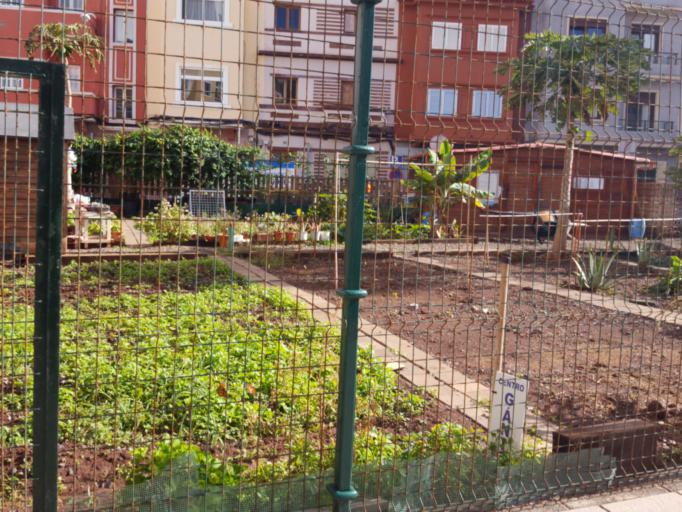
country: ES
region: Canary Islands
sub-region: Provincia de Las Palmas
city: Las Palmas de Gran Canaria
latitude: 28.1374
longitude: -15.4363
